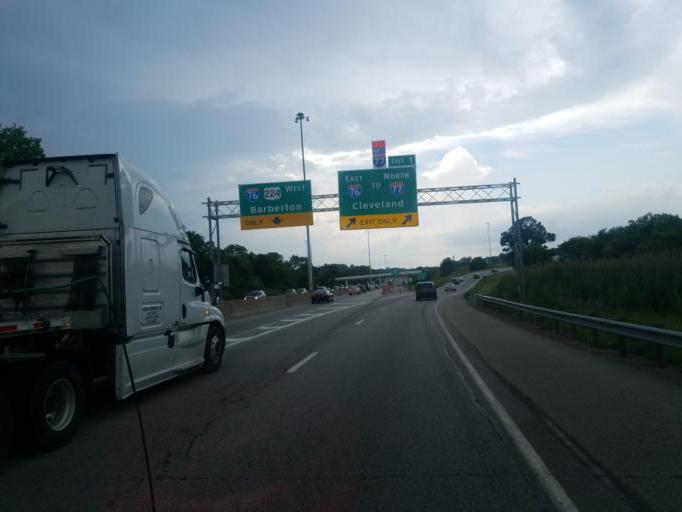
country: US
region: Ohio
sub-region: Summit County
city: Portage Lakes
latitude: 41.0356
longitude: -81.5618
